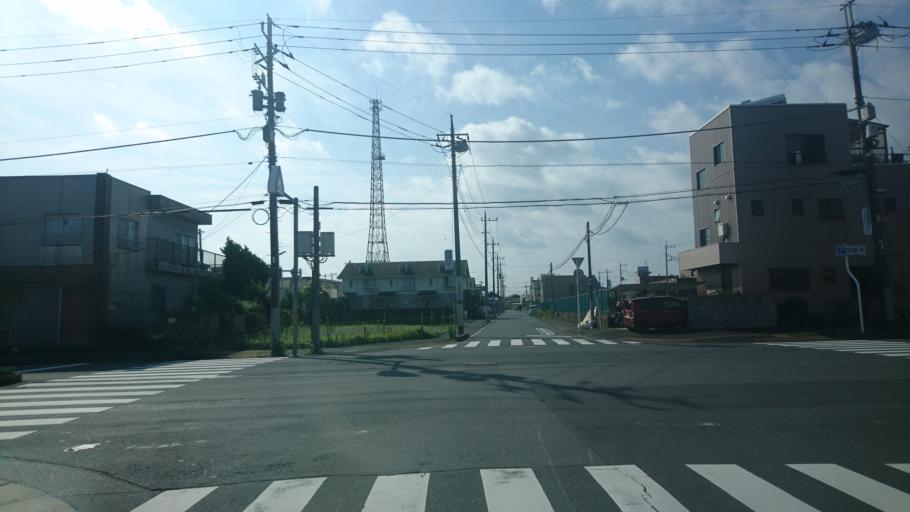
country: JP
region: Chiba
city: Katori-shi
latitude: 35.8968
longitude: 140.4943
